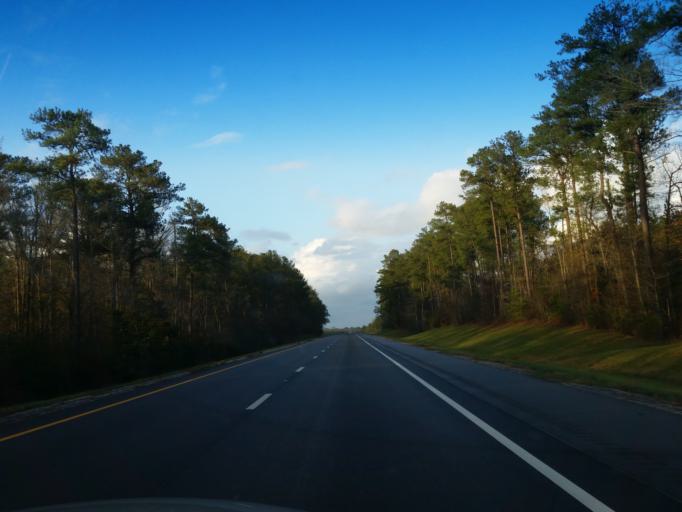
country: US
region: Mississippi
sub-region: Jones County
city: Sharon
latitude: 31.8573
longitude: -89.0472
